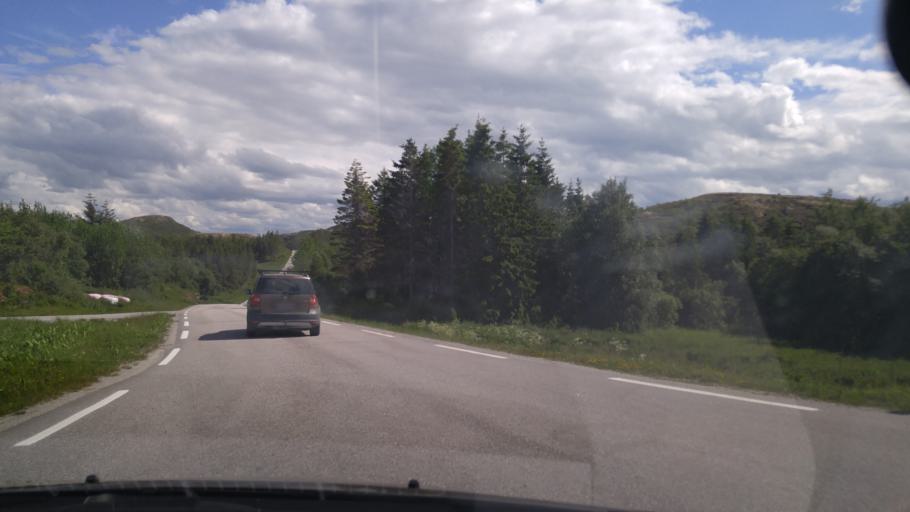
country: NO
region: Nord-Trondelag
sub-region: Vikna
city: Rorvik
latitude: 64.9033
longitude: 11.1559
